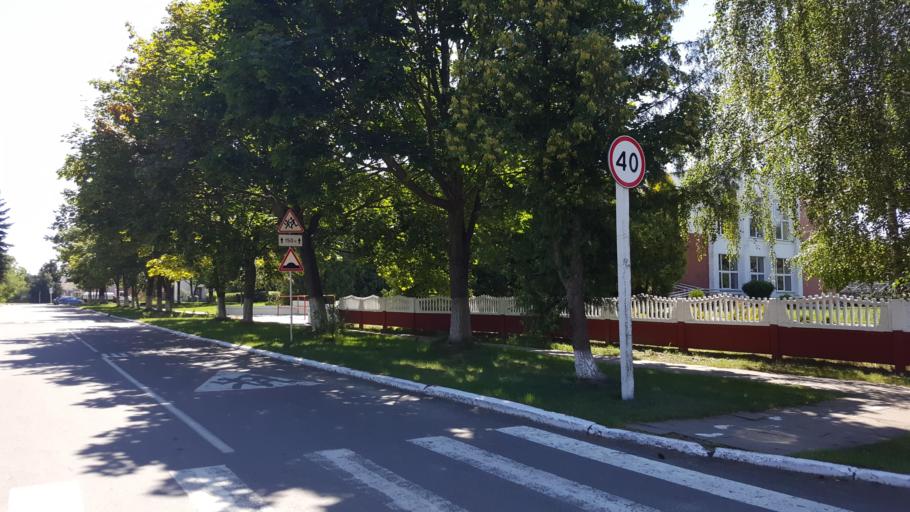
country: BY
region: Brest
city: Charnawchytsy
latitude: 52.2684
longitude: 23.5891
